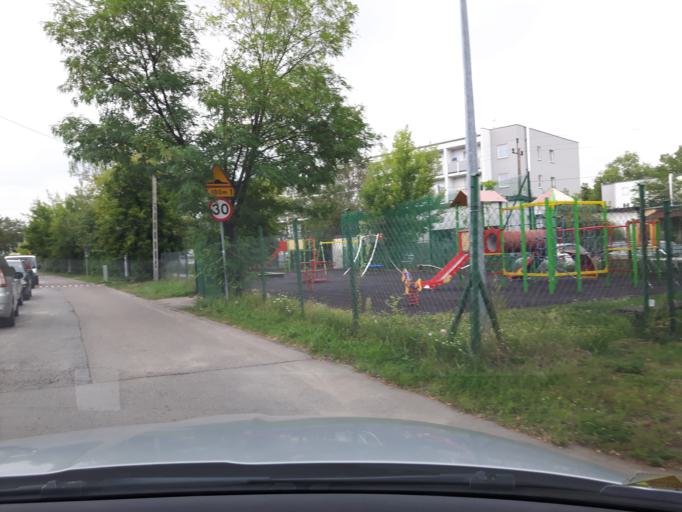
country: PL
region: Masovian Voivodeship
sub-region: Warszawa
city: Rembertow
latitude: 52.2430
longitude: 21.1326
